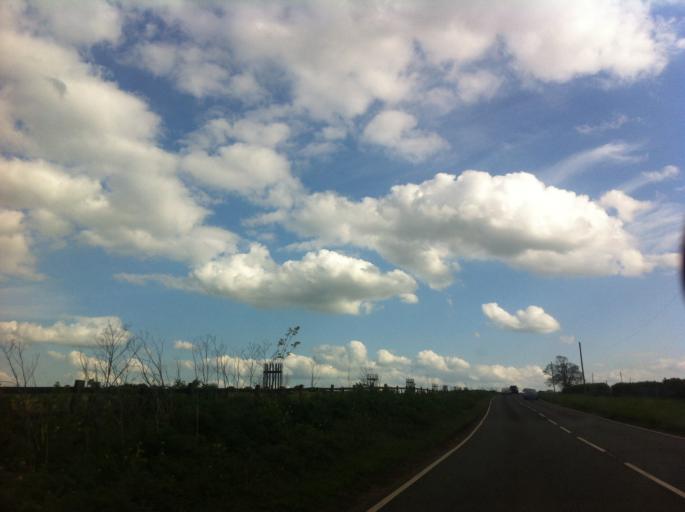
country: GB
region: England
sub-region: Northamptonshire
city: Irchester
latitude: 52.2746
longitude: -0.6769
